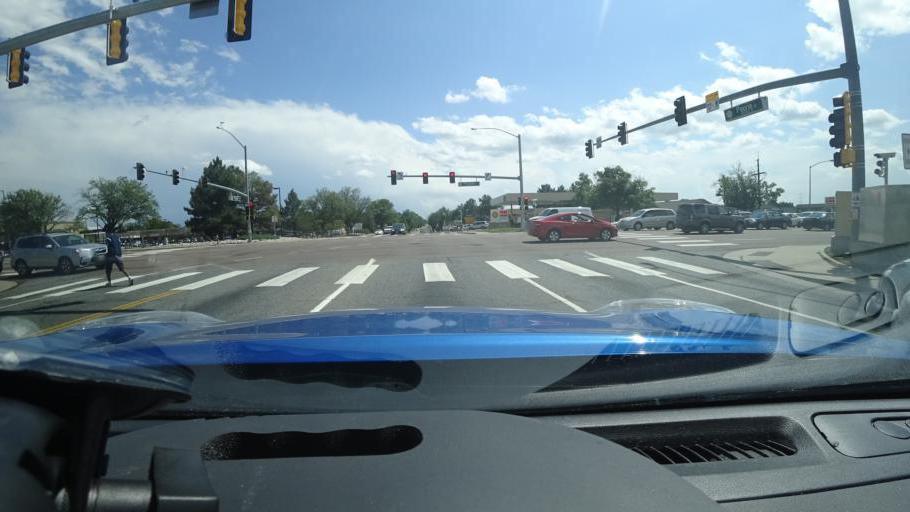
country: US
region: Colorado
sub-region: Adams County
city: Aurora
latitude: 39.6969
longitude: -104.8472
